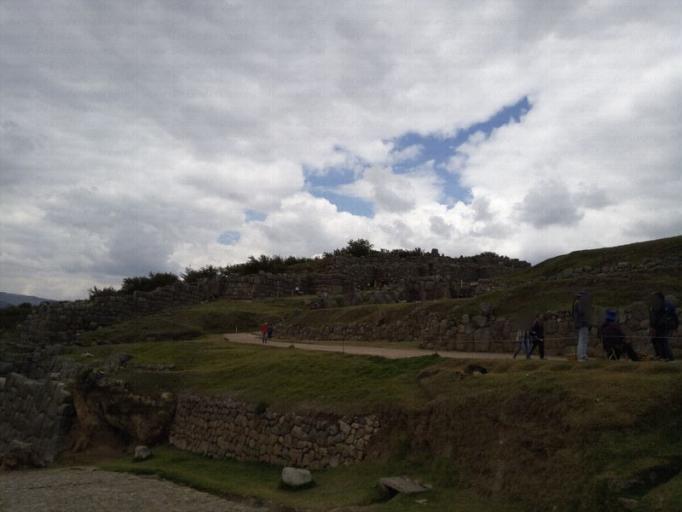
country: PE
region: Cusco
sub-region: Provincia de Cusco
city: Cusco
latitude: -13.5079
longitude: -71.9801
